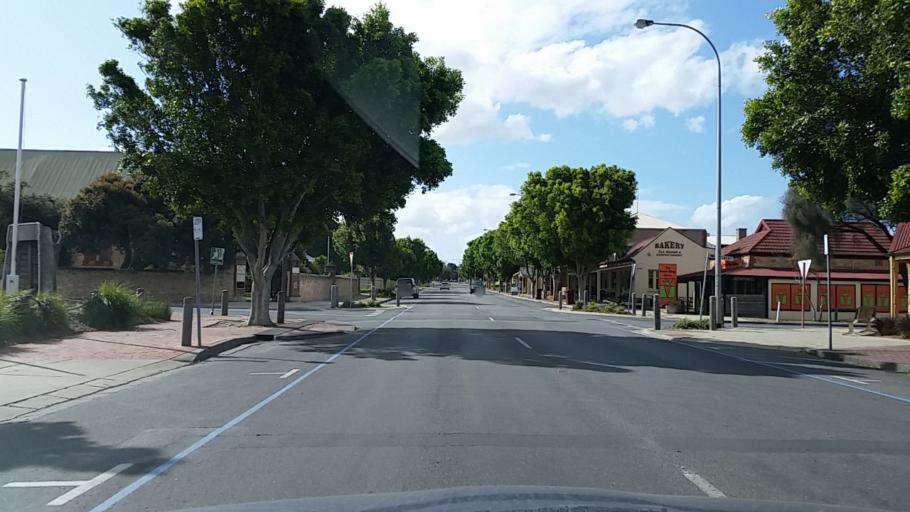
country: AU
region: South Australia
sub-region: Alexandrina
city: Goolwa
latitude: -35.5011
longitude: 138.7822
